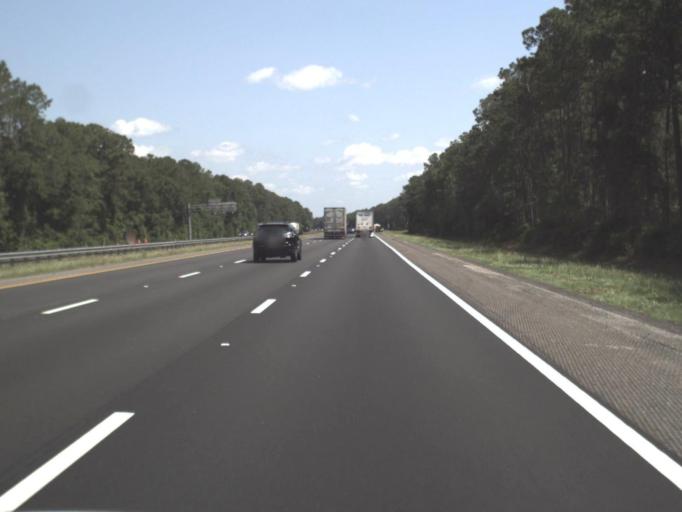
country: US
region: Florida
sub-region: Nassau County
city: Yulee
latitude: 30.5348
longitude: -81.6368
